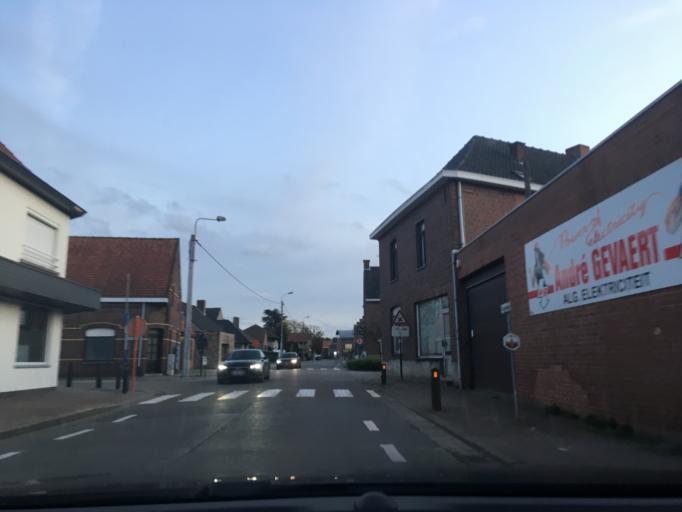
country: BE
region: Flanders
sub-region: Provincie West-Vlaanderen
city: Moorslede
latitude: 50.9393
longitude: 3.0586
